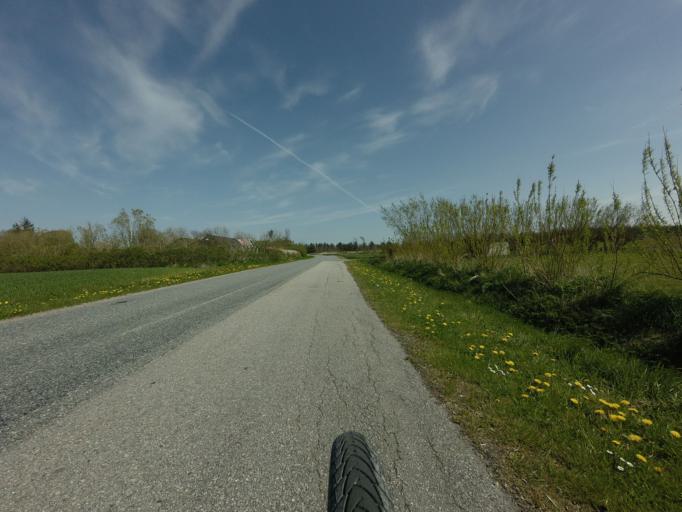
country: DK
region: North Denmark
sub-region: Jammerbugt Kommune
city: Pandrup
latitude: 57.2262
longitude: 9.6383
